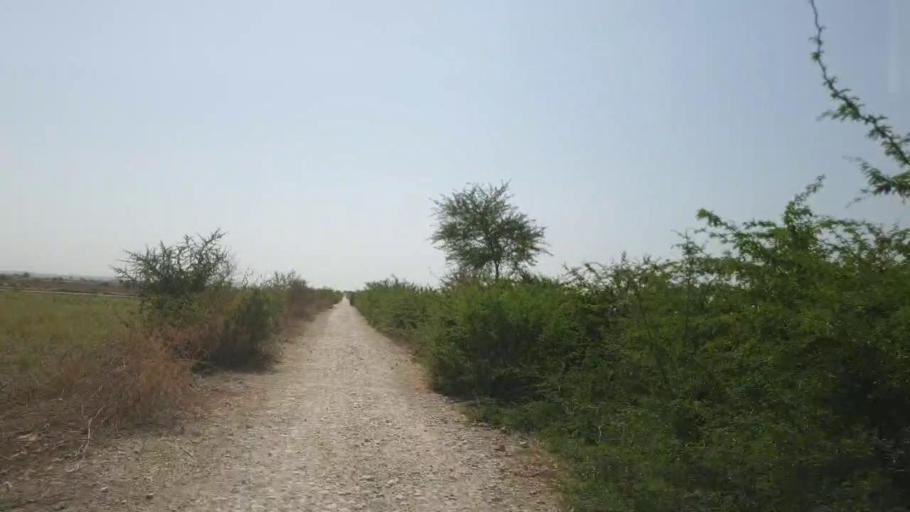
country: PK
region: Sindh
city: Naukot
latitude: 24.9173
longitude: 69.4878
